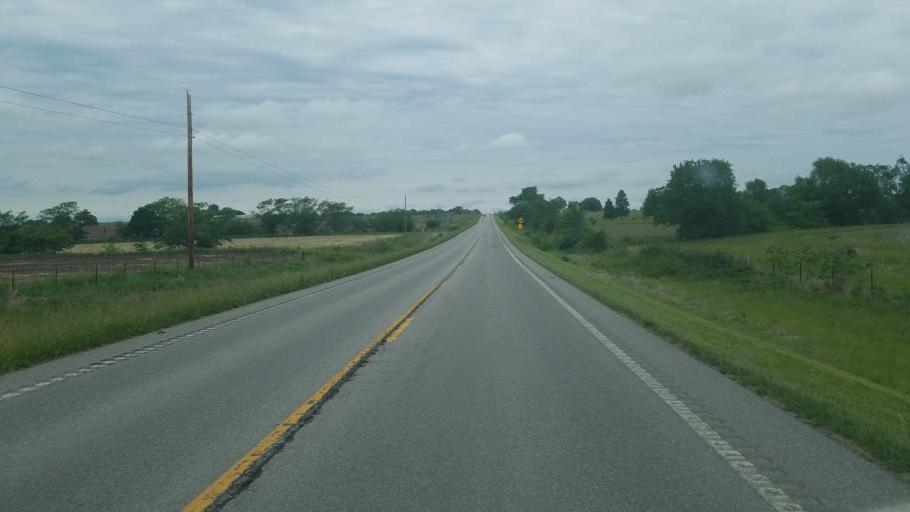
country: US
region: Missouri
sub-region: Morgan County
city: Versailles
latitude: 38.4508
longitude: -92.8093
